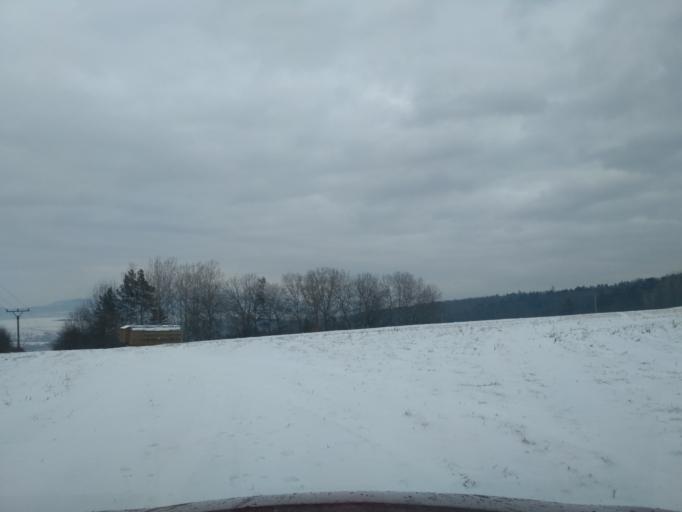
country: SK
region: Presovsky
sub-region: Okres Presov
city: Presov
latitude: 49.0030
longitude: 21.1531
